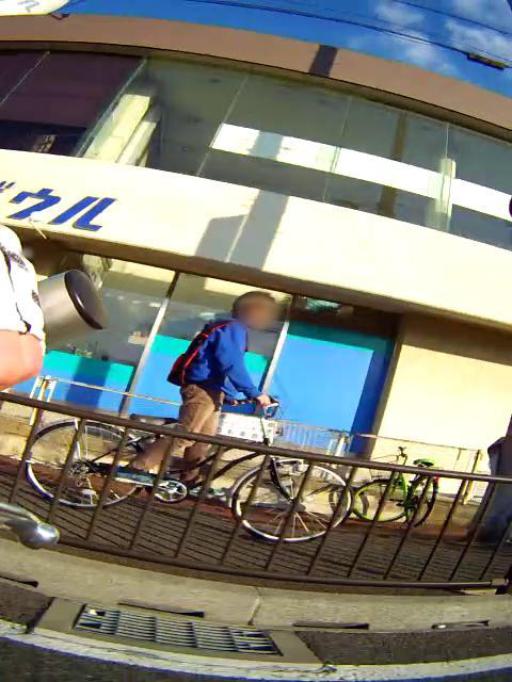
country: JP
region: Hyogo
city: Itami
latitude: 34.7605
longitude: 135.4118
